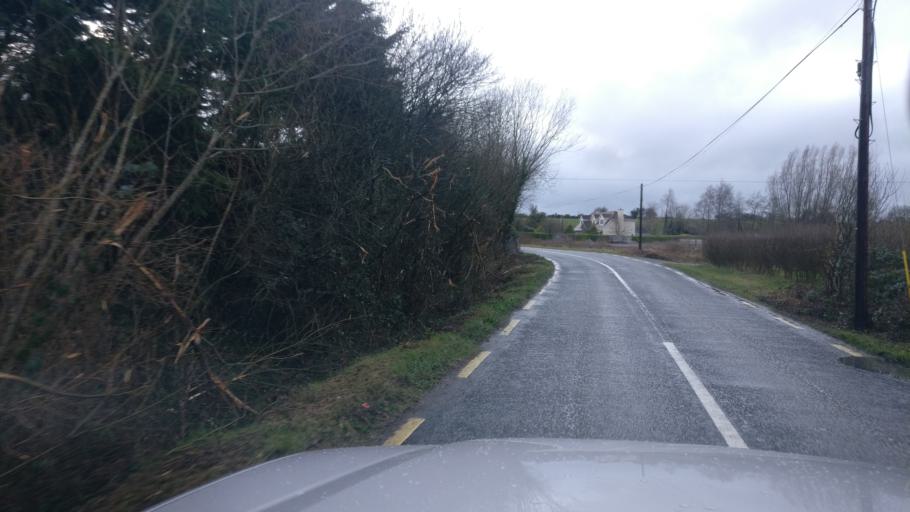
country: IE
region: Leinster
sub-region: An Iarmhi
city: Athlone
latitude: 53.4242
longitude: -8.0384
